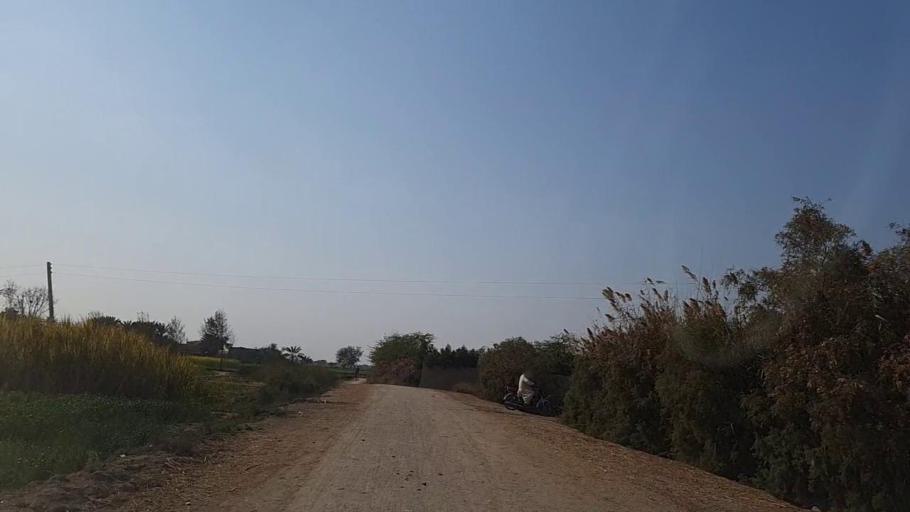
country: PK
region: Sindh
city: Daur
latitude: 26.4368
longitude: 68.2611
